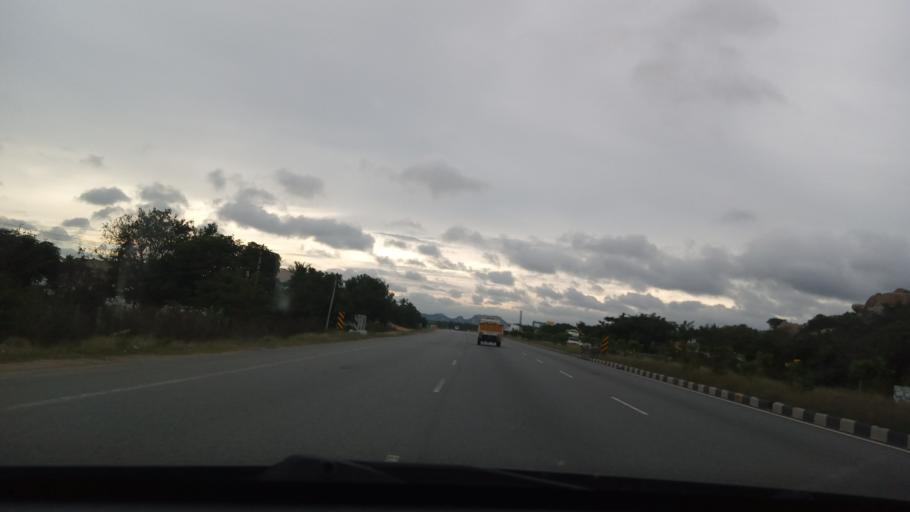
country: IN
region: Tamil Nadu
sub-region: Vellore
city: Jolarpettai
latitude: 12.5532
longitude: 78.4531
